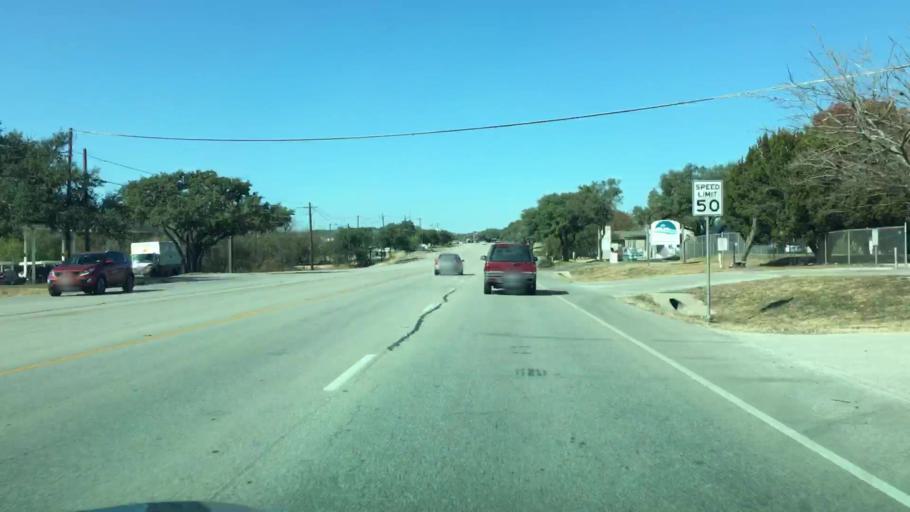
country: US
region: Texas
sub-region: Hays County
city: Dripping Springs
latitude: 30.1977
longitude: -98.1063
